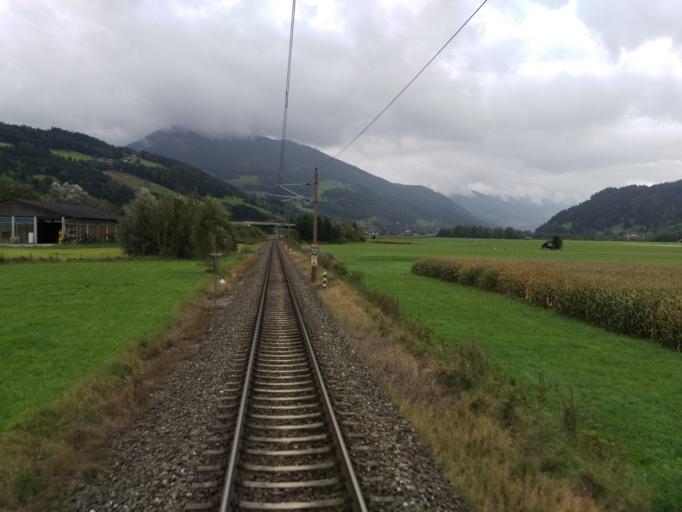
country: AT
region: Styria
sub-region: Politischer Bezirk Liezen
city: Niederoblarn
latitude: 47.4802
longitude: 14.0132
